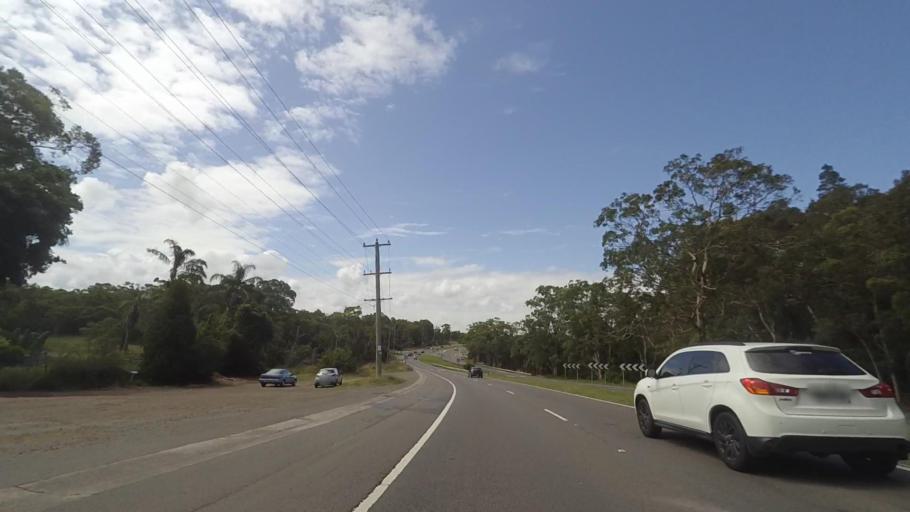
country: AU
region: New South Wales
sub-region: Lake Macquarie Shire
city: Windale
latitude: -33.0018
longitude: 151.6860
